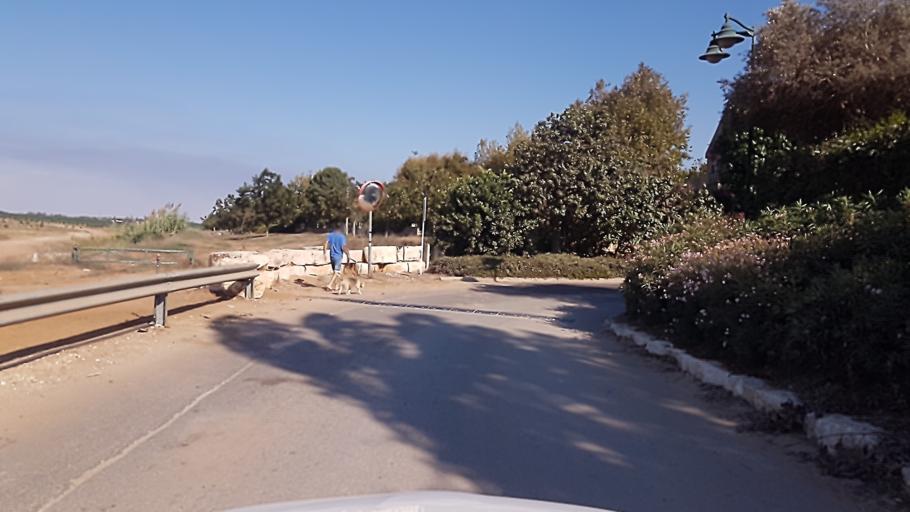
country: IL
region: Central District
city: Ra'anana
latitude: 32.2133
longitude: 34.8931
